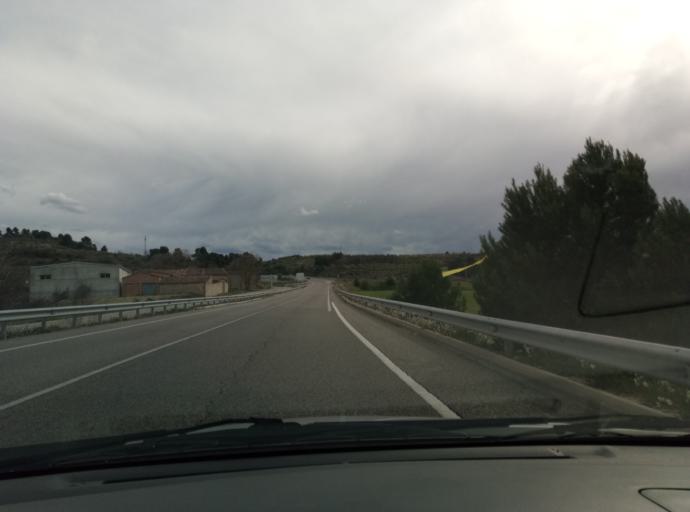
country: ES
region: Catalonia
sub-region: Provincia de Lleida
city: Ciutadilla
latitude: 41.5658
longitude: 1.1297
